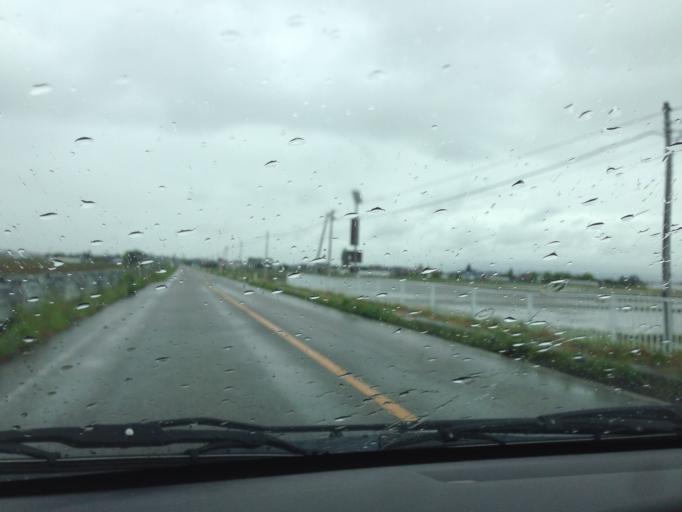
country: JP
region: Fukushima
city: Kitakata
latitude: 37.4796
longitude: 139.8396
